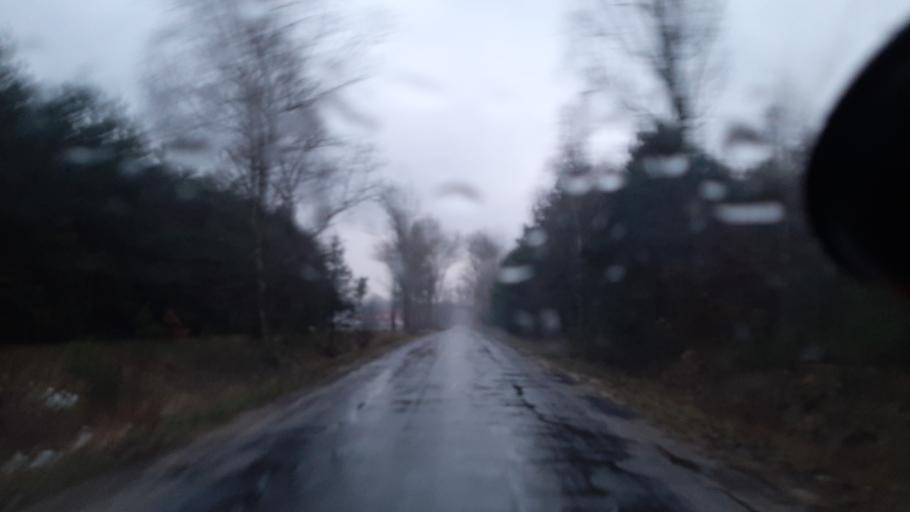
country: PL
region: Lublin Voivodeship
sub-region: Powiat lubartowski
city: Firlej
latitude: 51.5327
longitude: 22.5026
